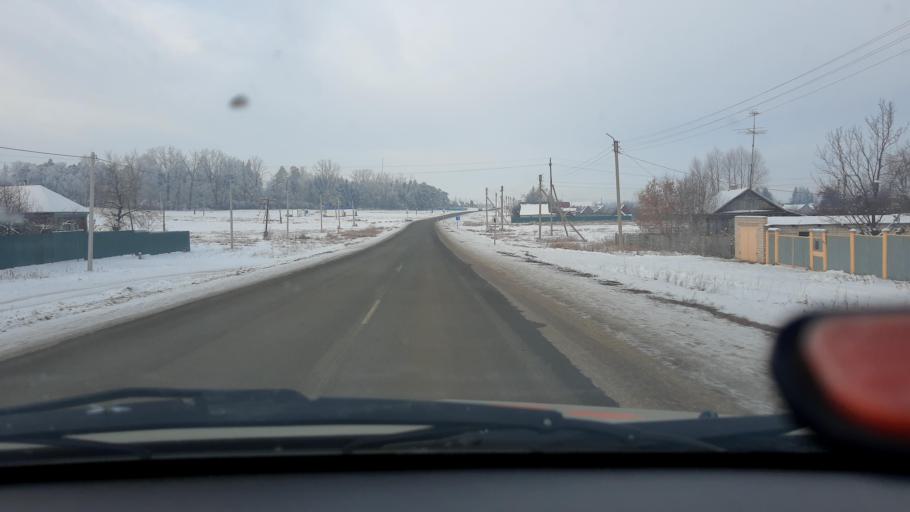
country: RU
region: Bashkortostan
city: Avdon
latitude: 54.3750
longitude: 55.8122
